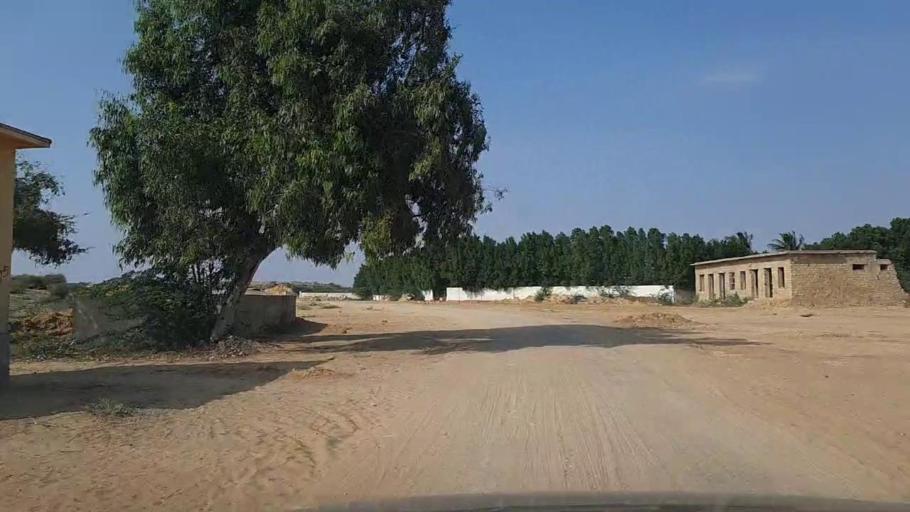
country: PK
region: Sindh
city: Gharo
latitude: 24.7673
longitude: 67.5768
